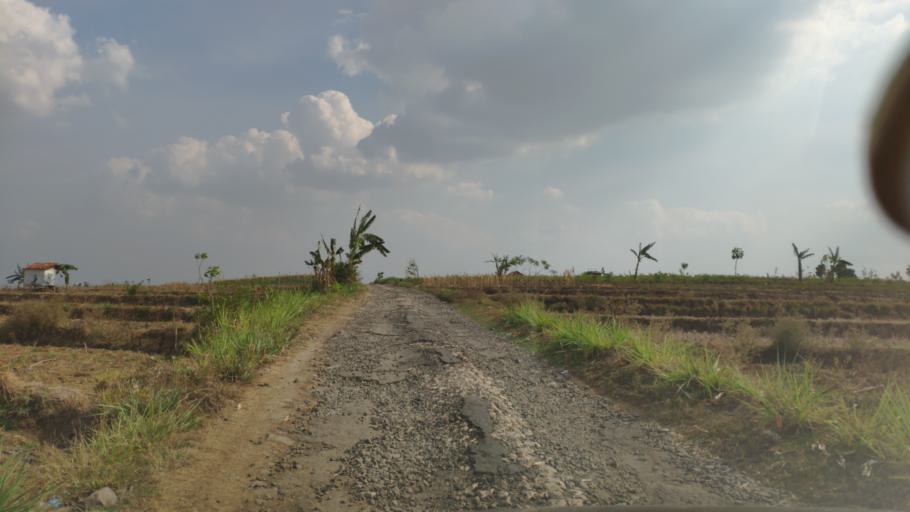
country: ID
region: Central Java
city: Ngapus
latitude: -6.9645
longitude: 111.1505
